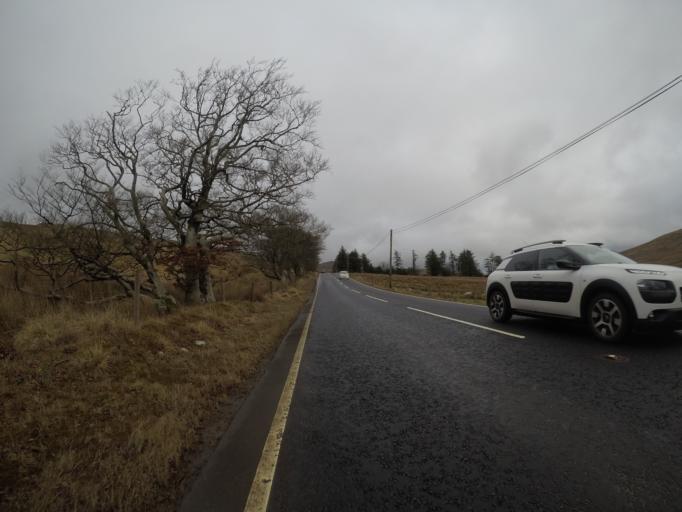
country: GB
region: Scotland
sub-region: North Ayrshire
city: Fairlie
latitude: 55.7778
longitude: -4.8145
